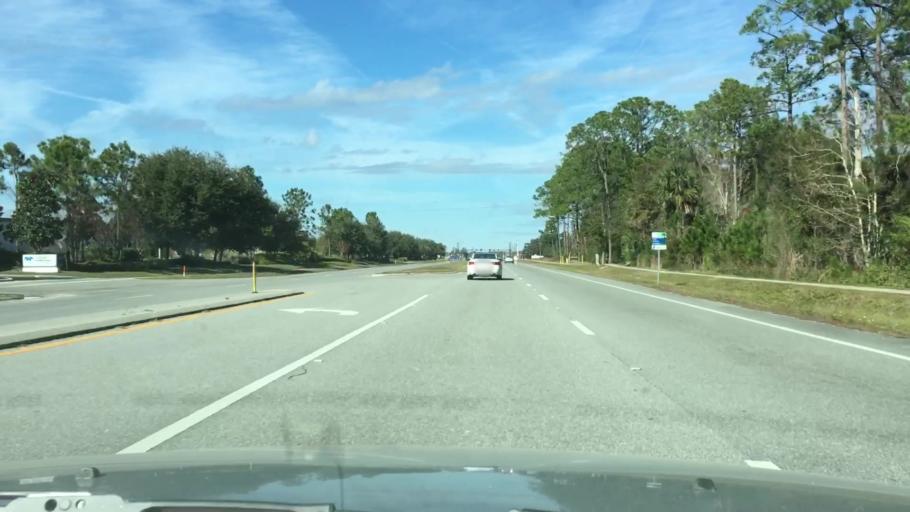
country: US
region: Florida
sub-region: Volusia County
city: Holly Hill
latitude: 29.2086
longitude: -81.0890
